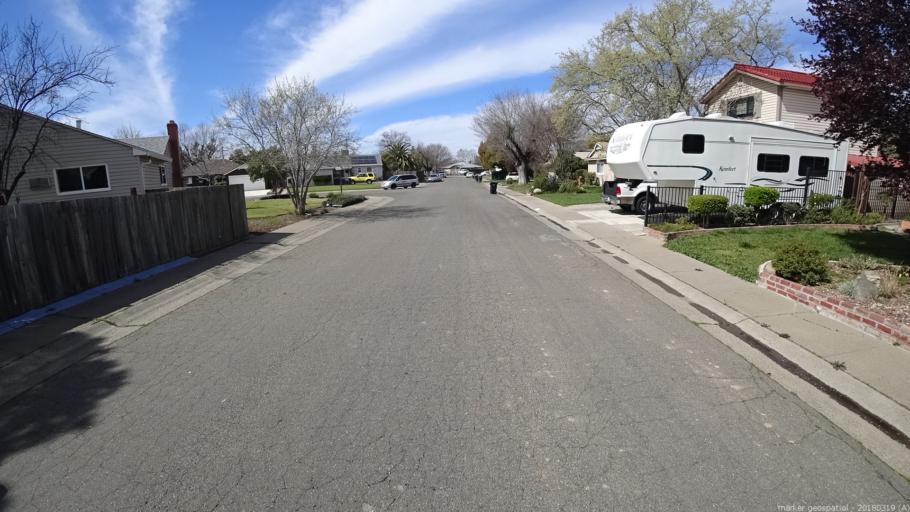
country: US
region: California
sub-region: Sacramento County
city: Parkway
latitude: 38.5060
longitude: -121.4442
